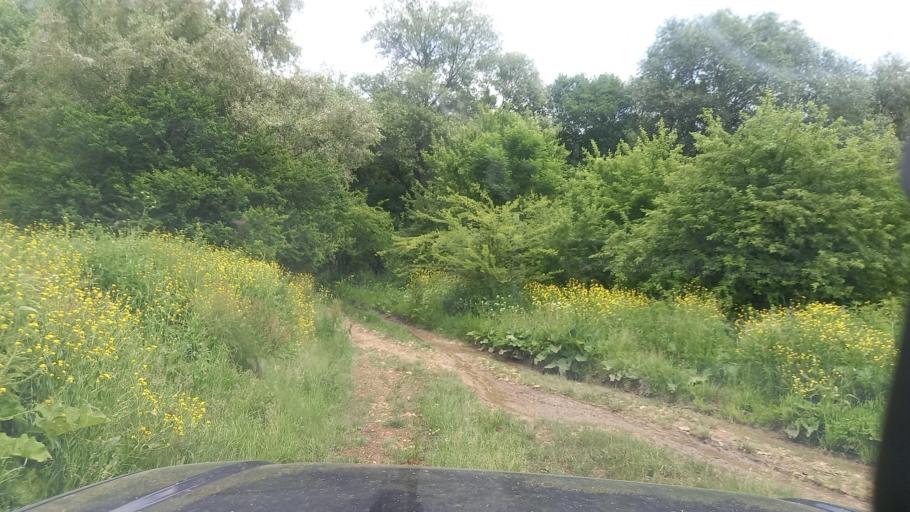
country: RU
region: Karachayevo-Cherkesiya
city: Pregradnaya
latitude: 44.0880
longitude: 41.1987
